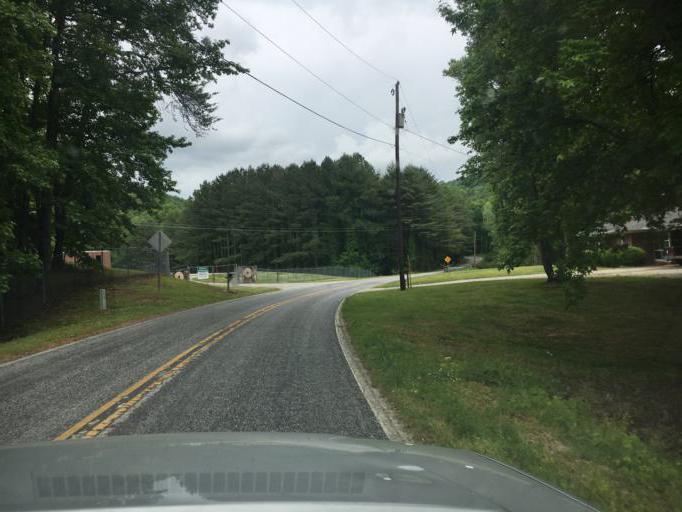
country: US
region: South Carolina
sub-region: Greenville County
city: Tigerville
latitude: 35.1366
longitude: -82.4122
